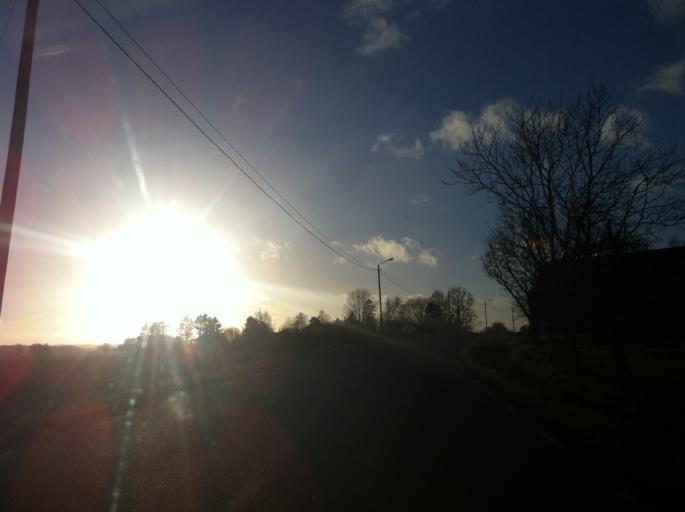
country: SE
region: Skane
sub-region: Hassleholms Kommun
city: Hastveda
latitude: 56.1985
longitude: 13.9270
